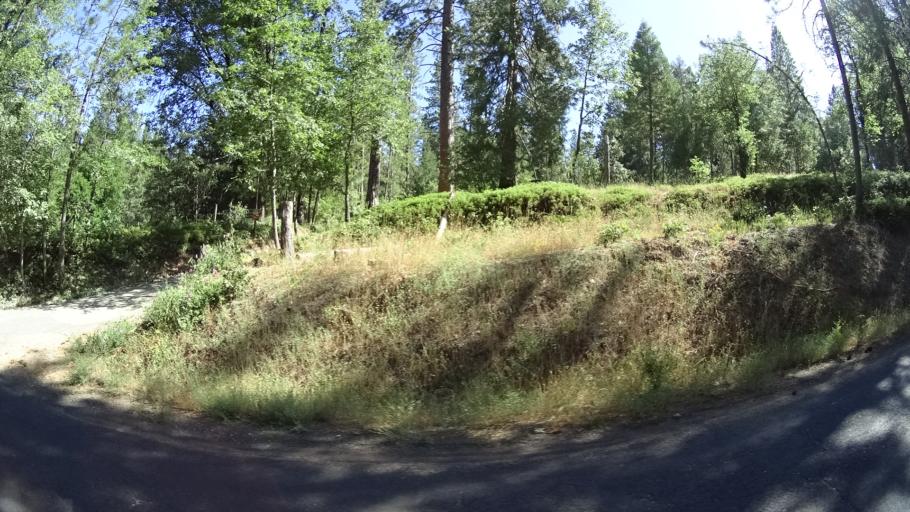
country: US
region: California
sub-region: Amador County
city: Pioneer
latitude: 38.4003
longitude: -120.5005
